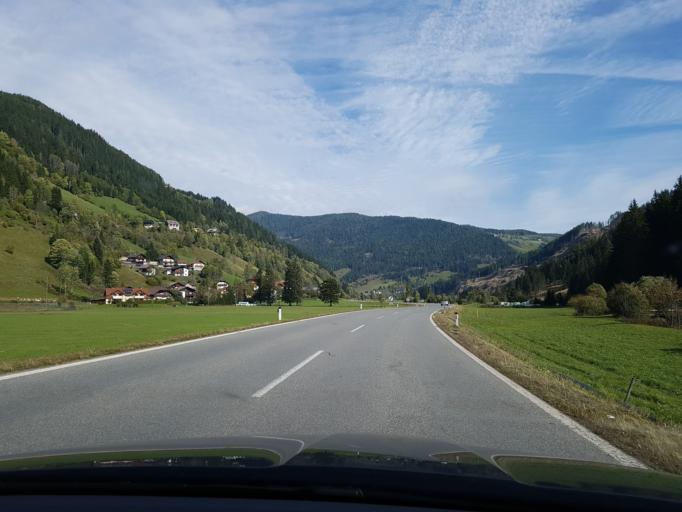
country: AT
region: Carinthia
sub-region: Politischer Bezirk Spittal an der Drau
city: Kleinkirchheim
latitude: 46.8398
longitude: 13.8756
